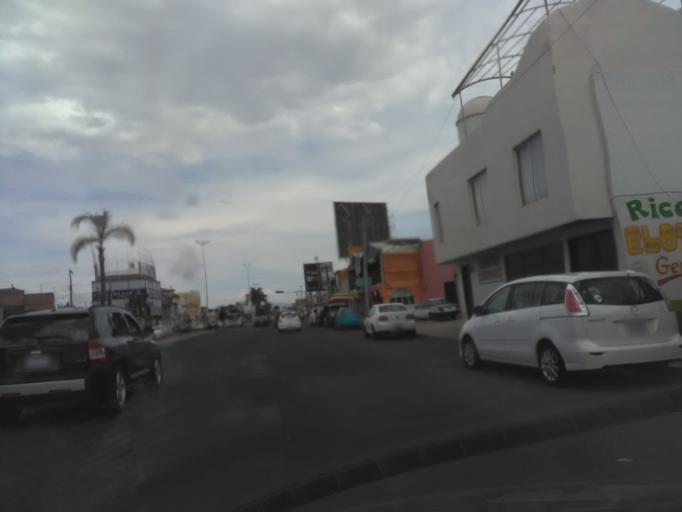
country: MX
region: Durango
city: Victoria de Durango
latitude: 24.0184
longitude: -104.6561
